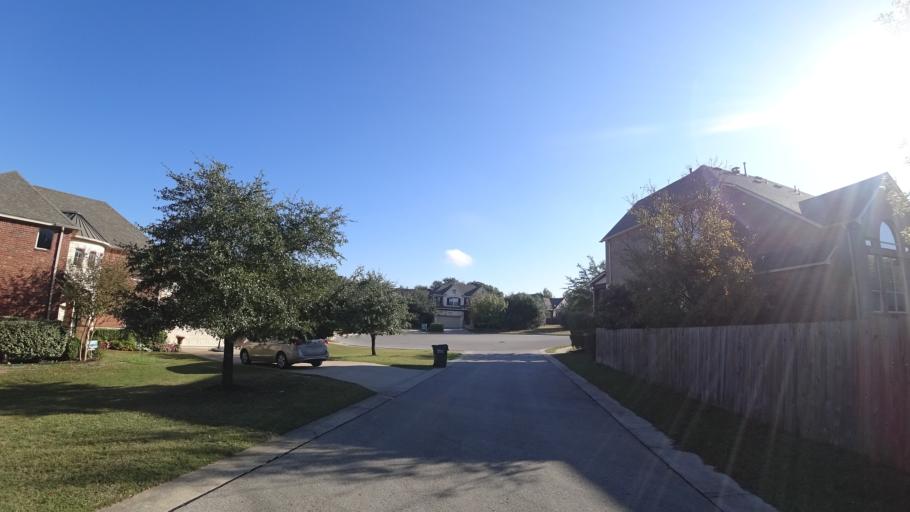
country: US
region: Texas
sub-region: Travis County
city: Hudson Bend
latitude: 30.3677
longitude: -97.8988
